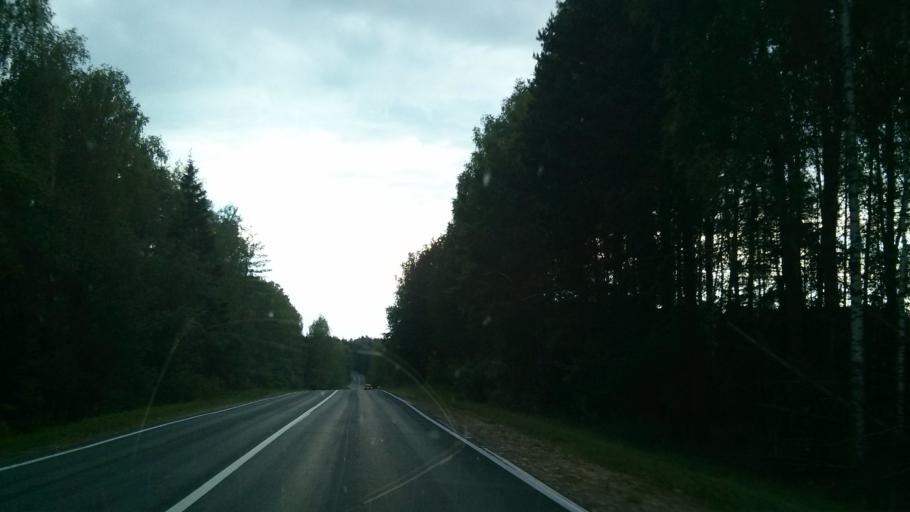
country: RU
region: Nizjnij Novgorod
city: Vacha
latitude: 55.7486
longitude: 42.4692
